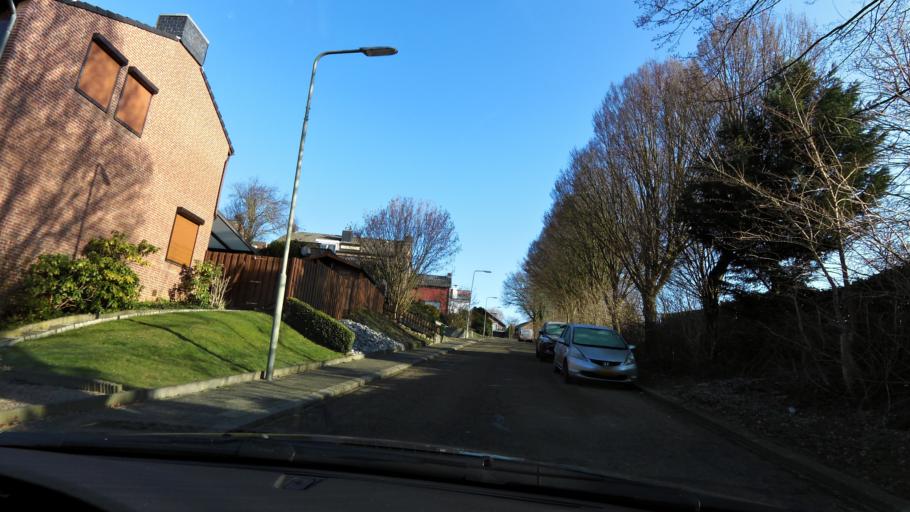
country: NL
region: Limburg
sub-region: Gemeente Simpelveld
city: Simpelveld
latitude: 50.8095
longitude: 5.9574
